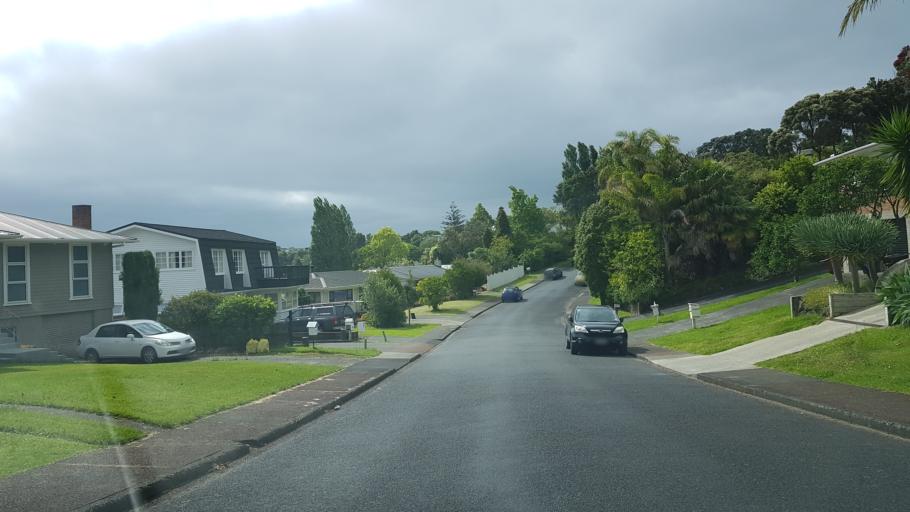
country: NZ
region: Auckland
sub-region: Auckland
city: North Shore
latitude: -36.8030
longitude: 174.7490
